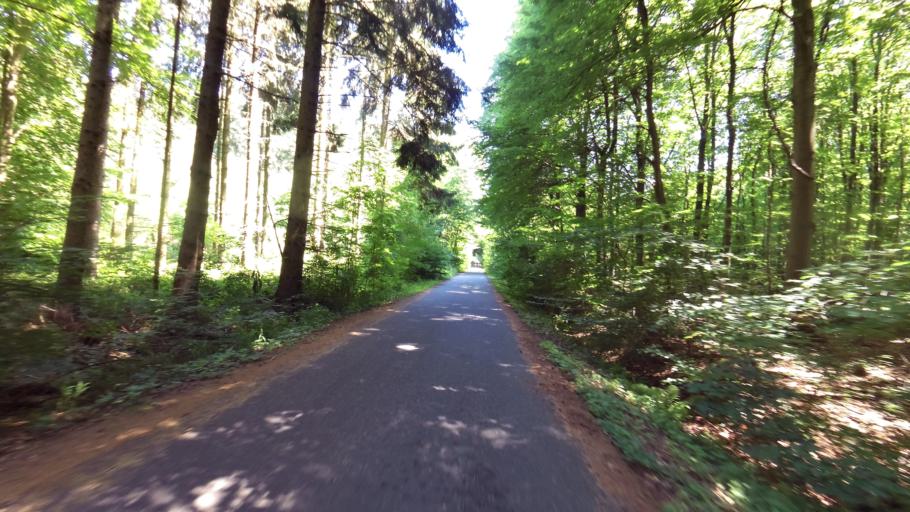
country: DE
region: North Rhine-Westphalia
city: Meckenheim
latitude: 50.6600
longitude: 7.0401
